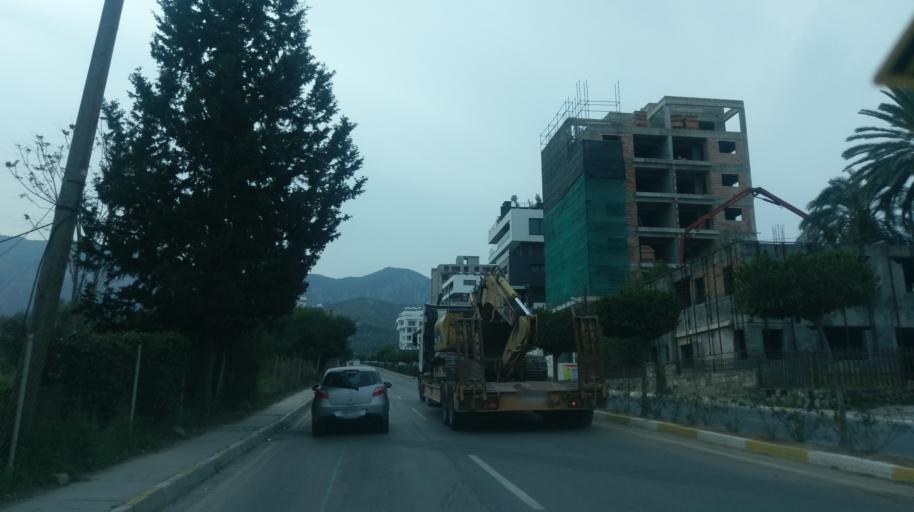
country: CY
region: Keryneia
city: Kyrenia
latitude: 35.3305
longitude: 33.3194
